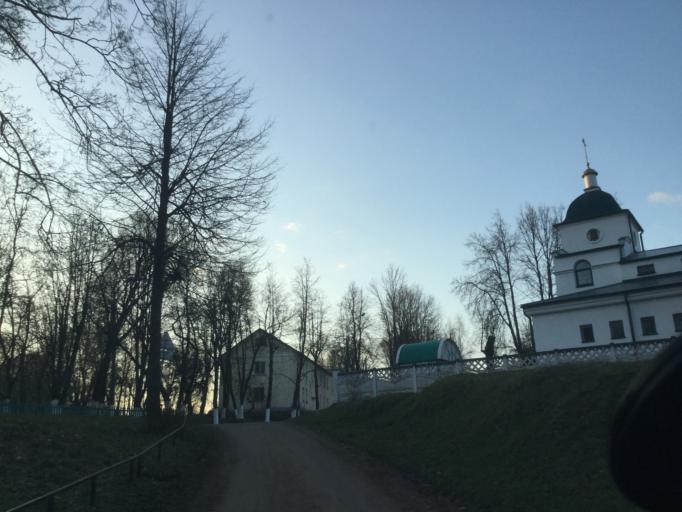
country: BY
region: Vitebsk
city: Vitebsk
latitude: 55.1648
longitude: 30.1313
